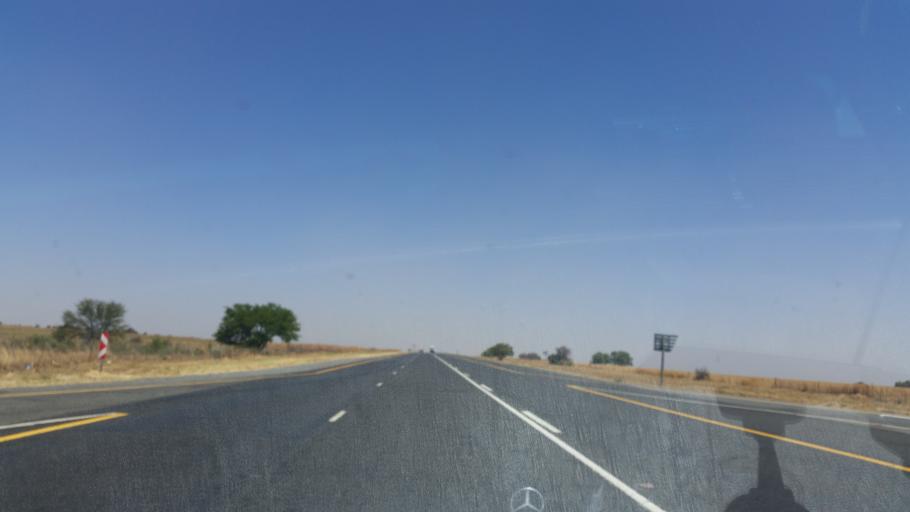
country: ZA
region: Orange Free State
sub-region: Lejweleputswa District Municipality
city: Winburg
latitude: -28.6428
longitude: 26.8871
